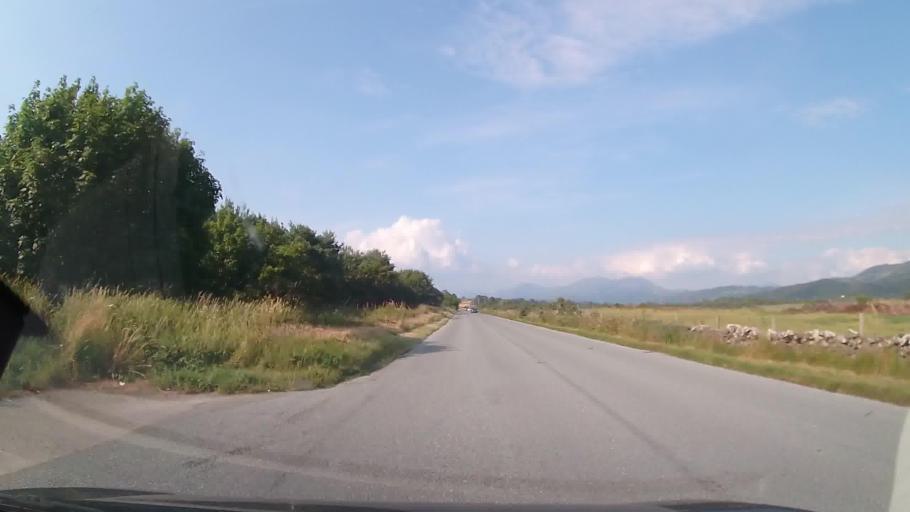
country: GB
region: Wales
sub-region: Gwynedd
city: Llanfair
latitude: 52.8796
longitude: -4.1030
